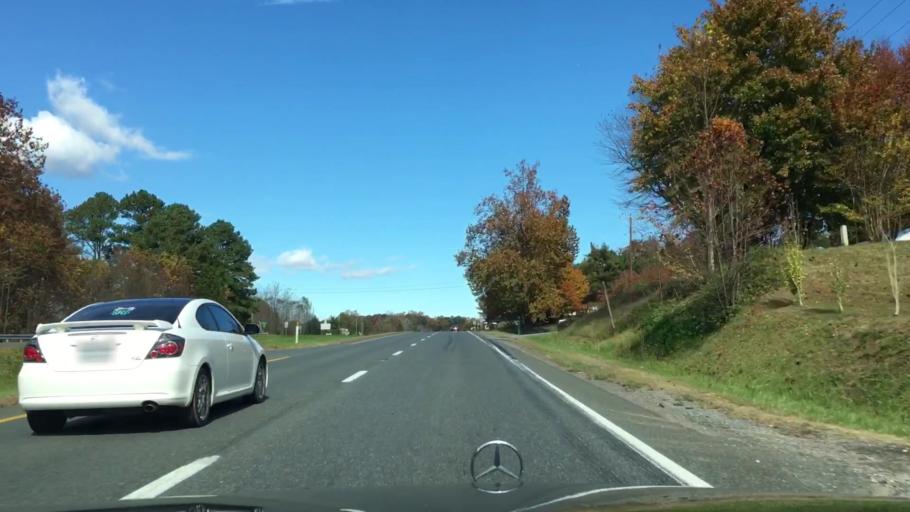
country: US
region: Virginia
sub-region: Campbell County
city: Altavista
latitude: 37.1963
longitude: -79.2035
